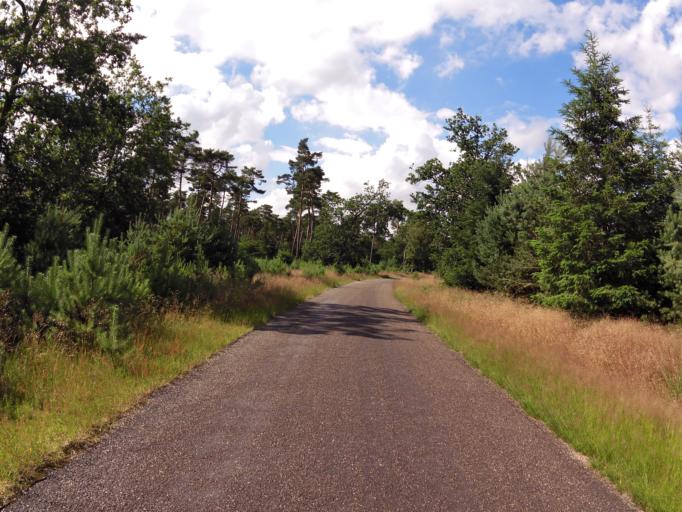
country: NL
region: North Brabant
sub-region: Gemeente Valkenswaard
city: Valkenswaard
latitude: 51.3385
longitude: 5.5080
